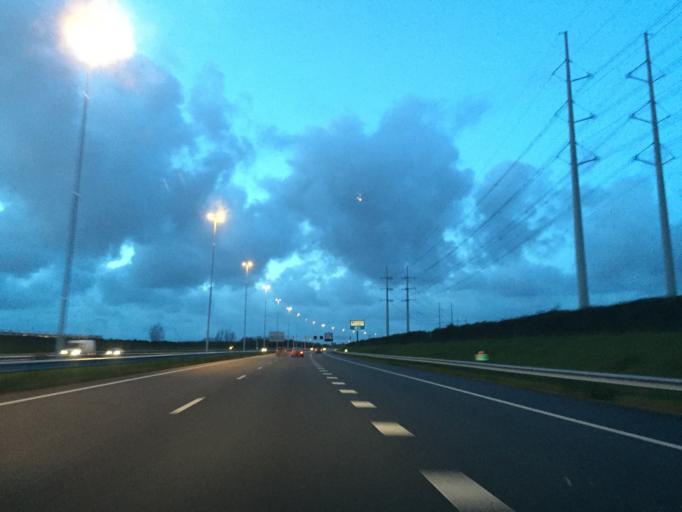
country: NL
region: South Holland
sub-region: Gemeente Rijswijk
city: Rijswijk
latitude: 51.9984
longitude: 4.3154
